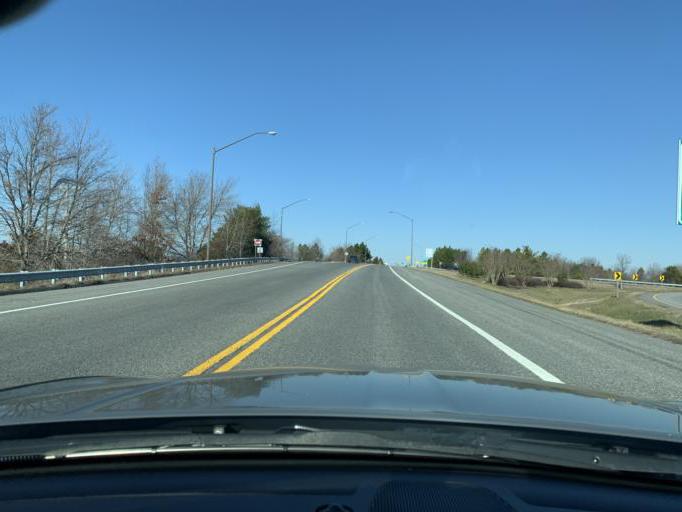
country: US
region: Maryland
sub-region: Queen Anne's County
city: Centreville
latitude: 39.0119
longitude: -76.0758
